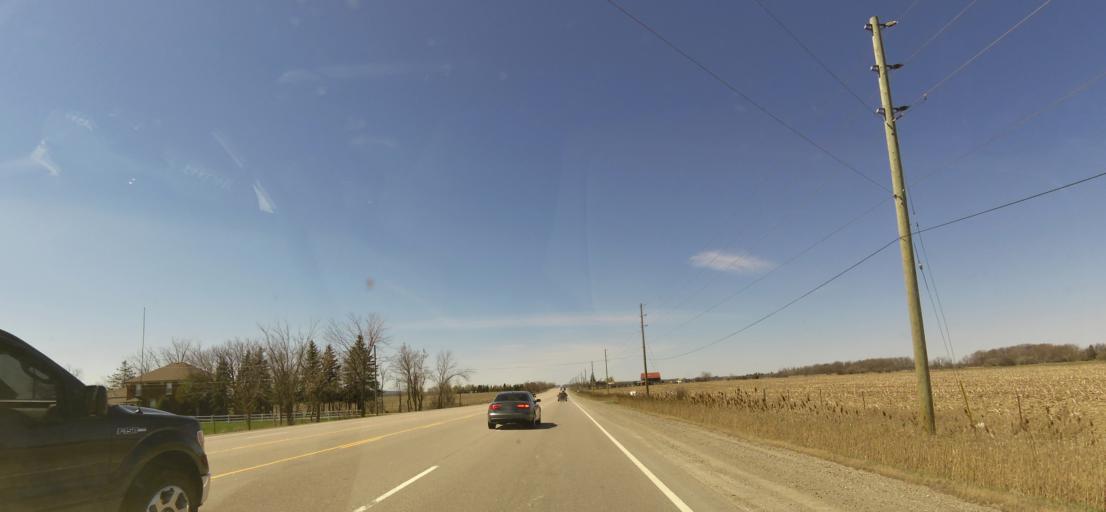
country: CA
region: Ontario
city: Brampton
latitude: 43.7580
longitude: -79.8571
